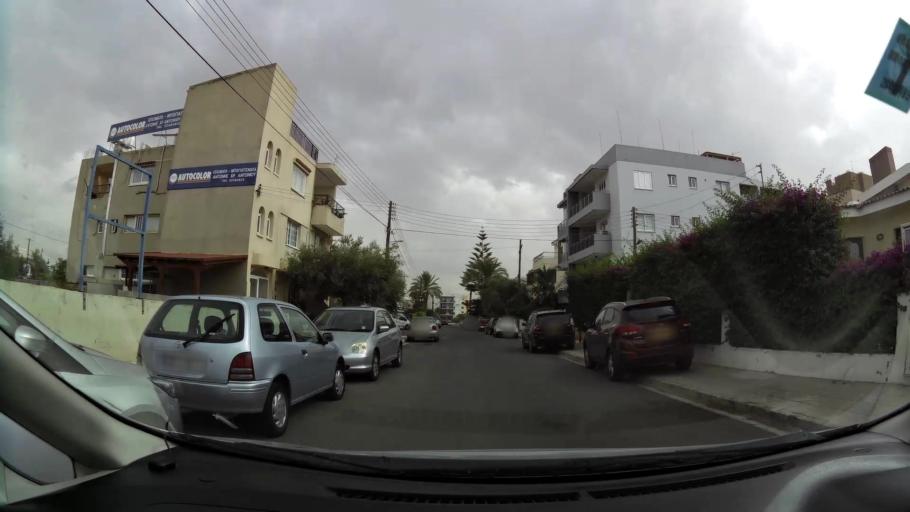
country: CY
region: Lefkosia
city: Geri
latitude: 35.1062
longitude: 33.3818
